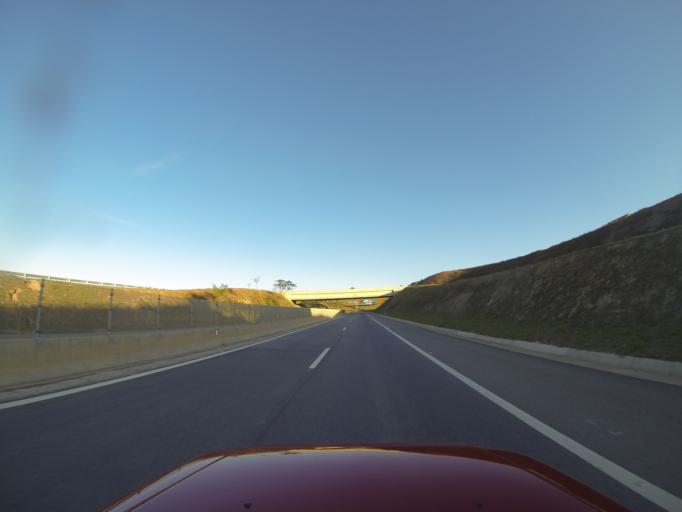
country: BR
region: Sao Paulo
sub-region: Santa Branca
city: Santa Branca
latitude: -23.4214
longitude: -45.6376
